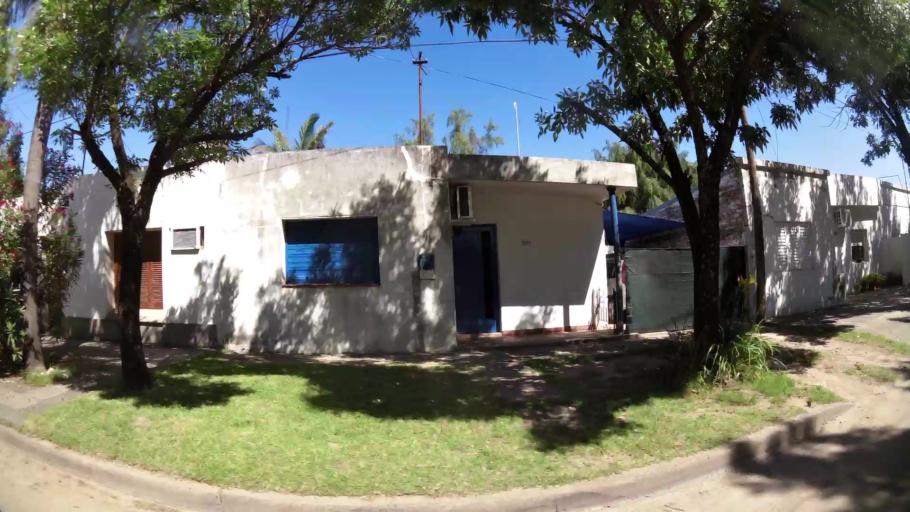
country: AR
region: Santa Fe
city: Esperanza
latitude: -31.4395
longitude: -60.9304
